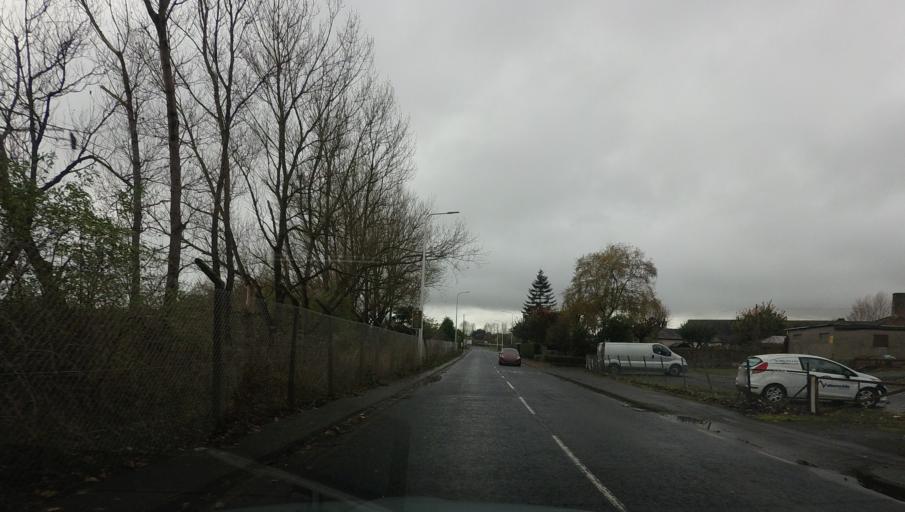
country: GB
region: Scotland
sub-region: Fife
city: Kirkcaldy
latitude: 56.1331
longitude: -3.1167
